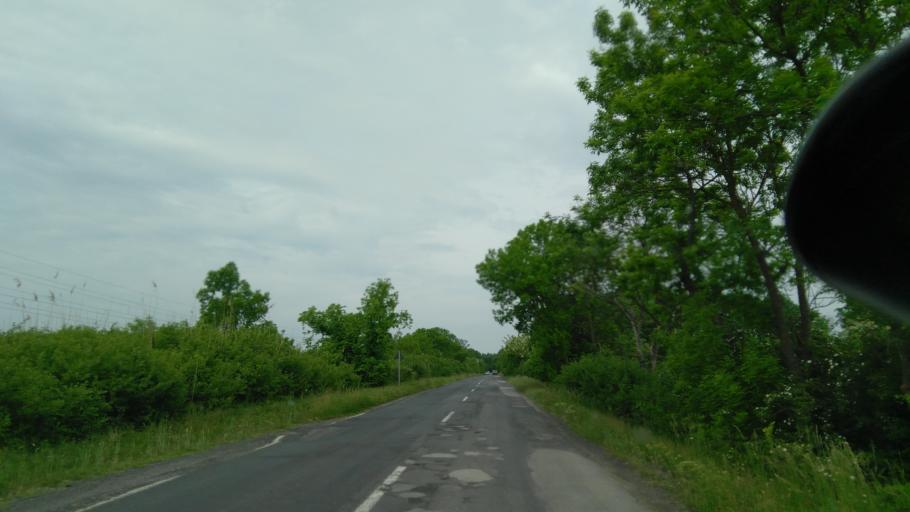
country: HU
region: Bekes
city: Szeghalom
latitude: 46.9742
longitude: 21.1976
